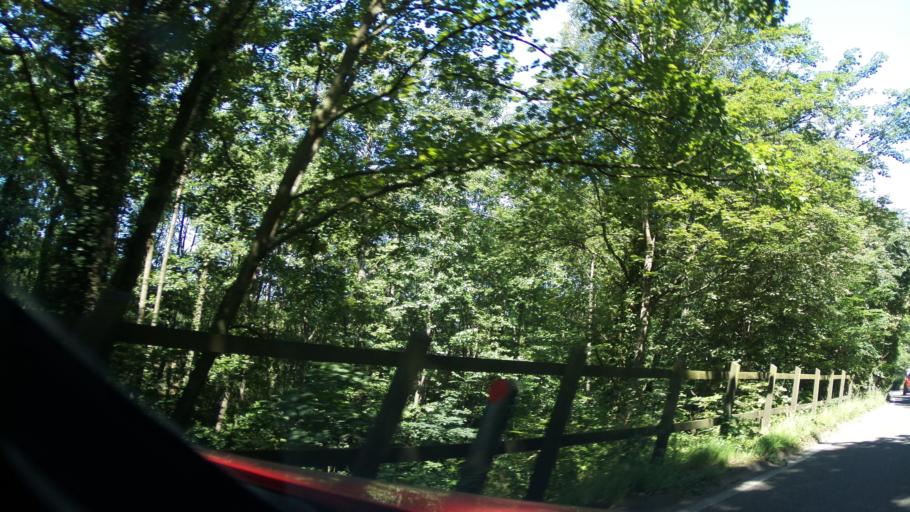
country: GB
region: England
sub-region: Derbyshire
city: Bakewell
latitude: 53.1863
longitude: -1.6115
